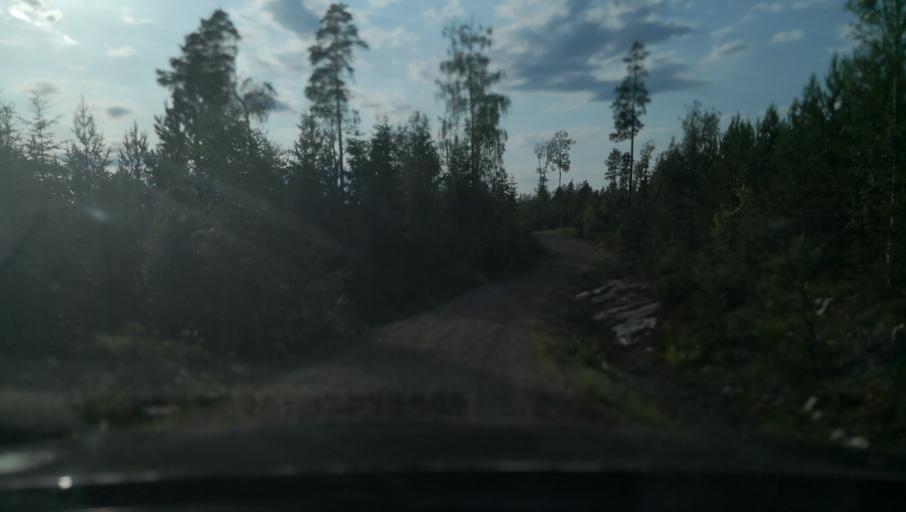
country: SE
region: Dalarna
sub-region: Smedjebackens Kommun
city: Smedjebacken
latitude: 60.0683
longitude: 15.3060
